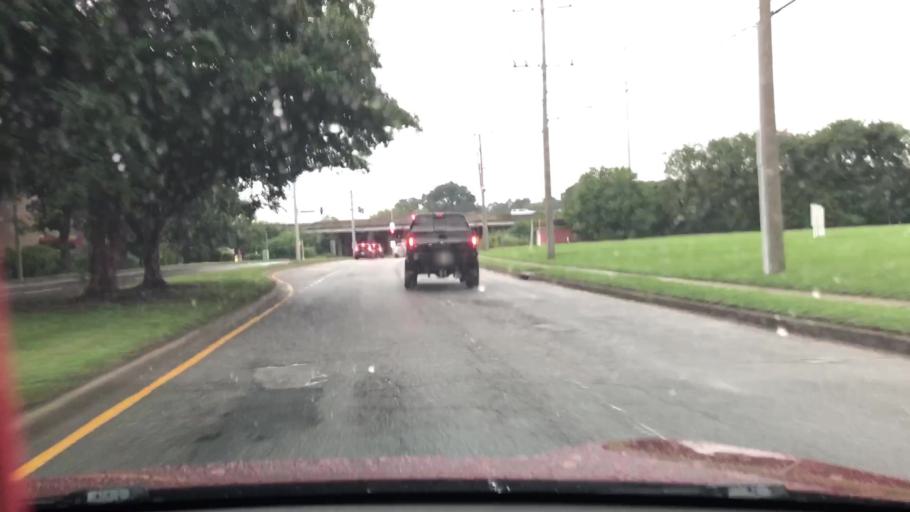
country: US
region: Virginia
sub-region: City of Chesapeake
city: Chesapeake
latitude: 36.8475
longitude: -76.1910
